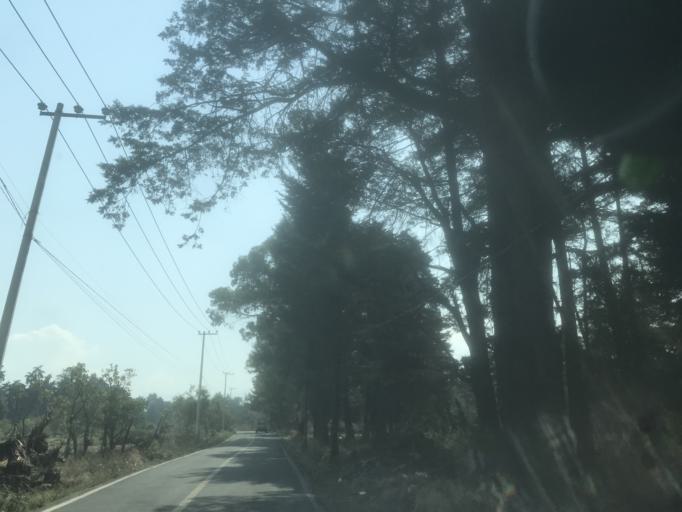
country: MX
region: Mexico
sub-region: Atlautla
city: San Juan Tepecoculco
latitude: 18.9957
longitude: -98.7841
